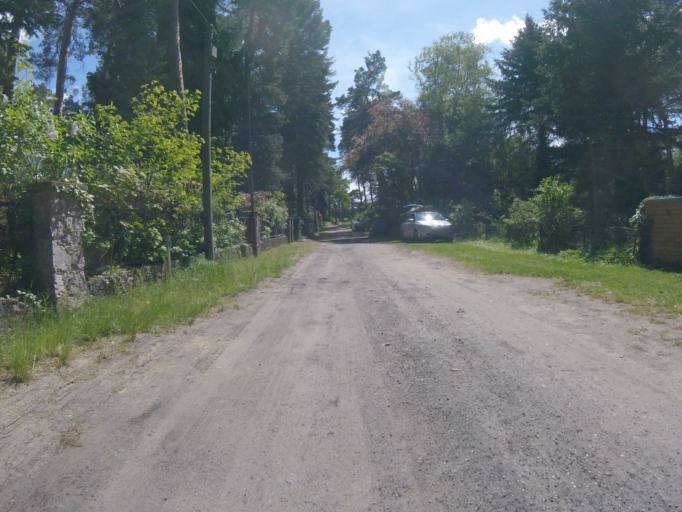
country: DE
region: Brandenburg
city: Teupitz
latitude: 52.1427
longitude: 13.5937
